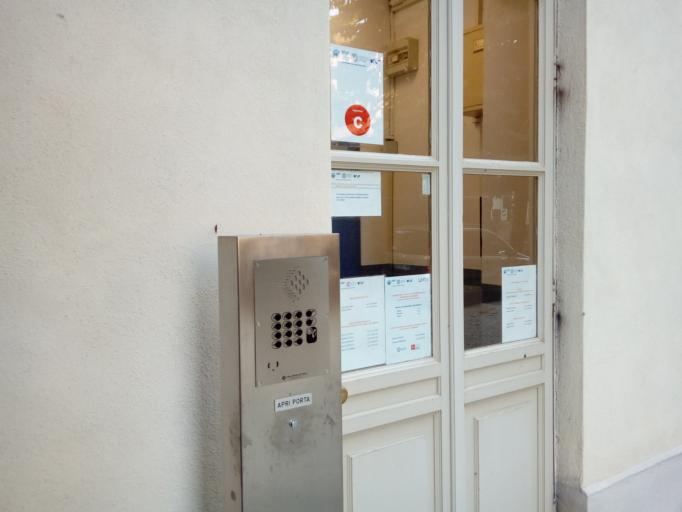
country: IT
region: Piedmont
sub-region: Provincia di Torino
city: Turin
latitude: 45.0534
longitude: 7.6864
